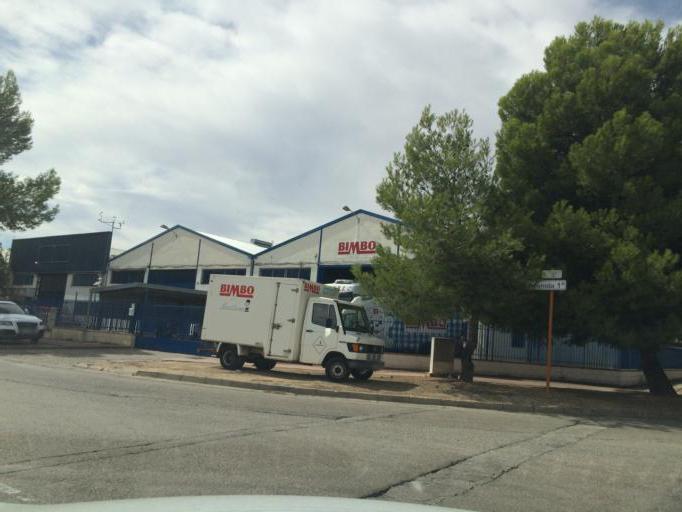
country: ES
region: Castille-La Mancha
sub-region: Provincia de Albacete
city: Albacete
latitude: 39.0234
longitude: -1.8805
